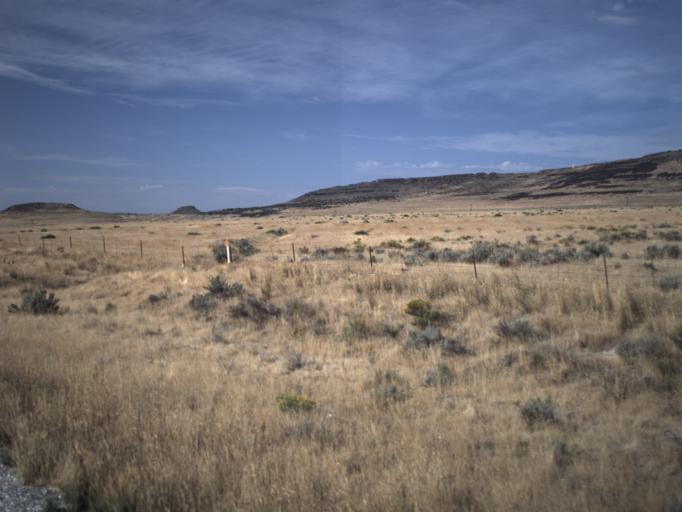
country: US
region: Idaho
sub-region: Minidoka County
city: Rupert
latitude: 41.8581
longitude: -113.1302
